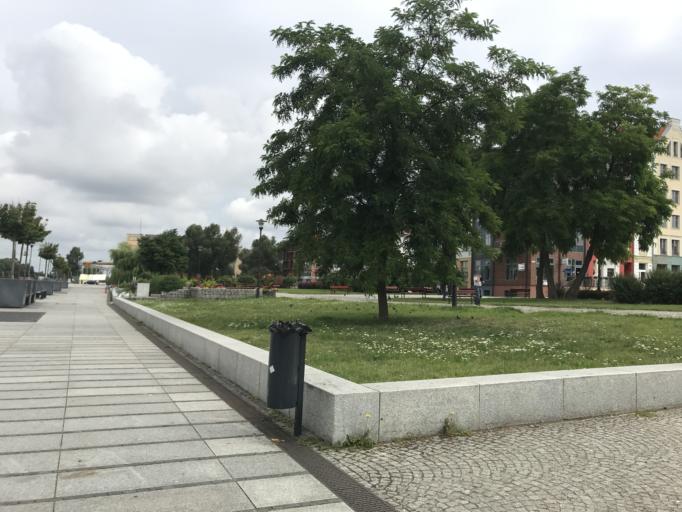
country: PL
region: Warmian-Masurian Voivodeship
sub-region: Powiat elblaski
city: Elblag
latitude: 54.1583
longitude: 19.3925
